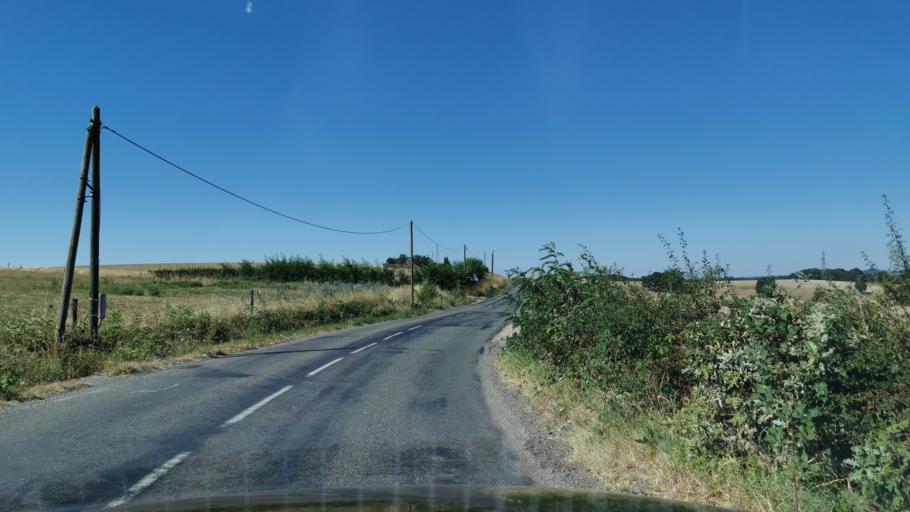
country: FR
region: Bourgogne
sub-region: Departement de Saone-et-Loire
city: Le Breuil
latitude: 46.7857
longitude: 4.4842
